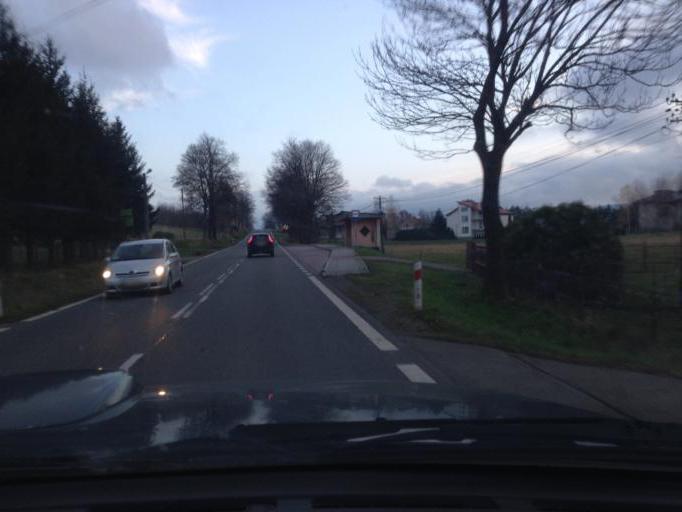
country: PL
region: Subcarpathian Voivodeship
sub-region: Powiat jasielski
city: Nowy Zmigrod
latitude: 49.6320
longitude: 21.5287
